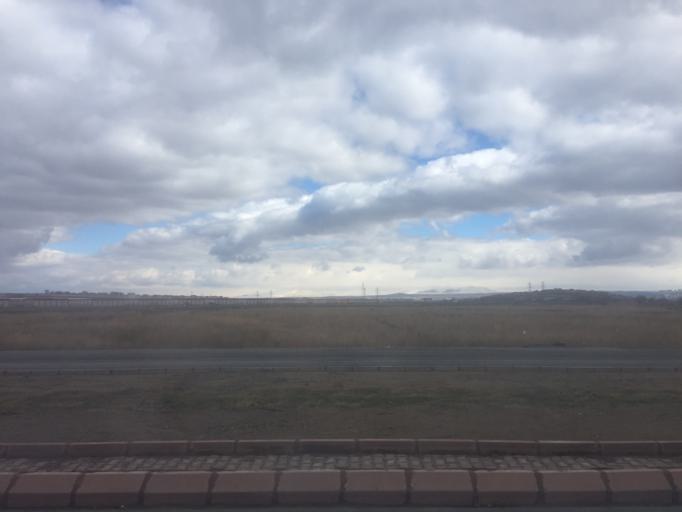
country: TR
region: Kayseri
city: Melikgazi
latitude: 38.7735
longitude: 35.4128
